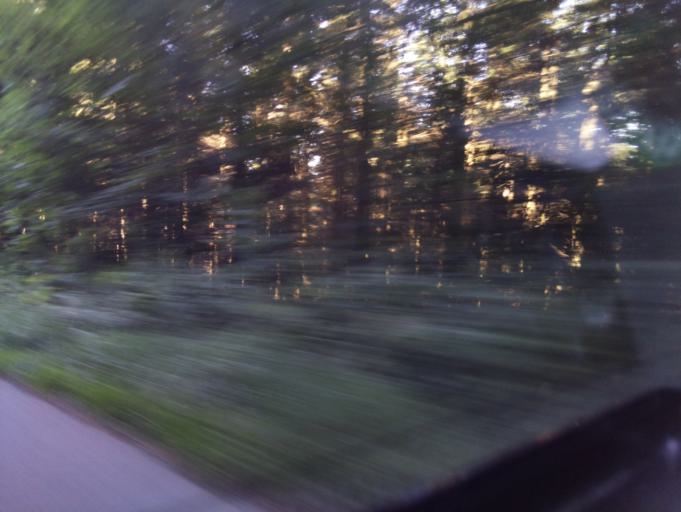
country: GB
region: Wales
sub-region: Monmouthshire
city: Tintern
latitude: 51.6743
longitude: -2.7522
